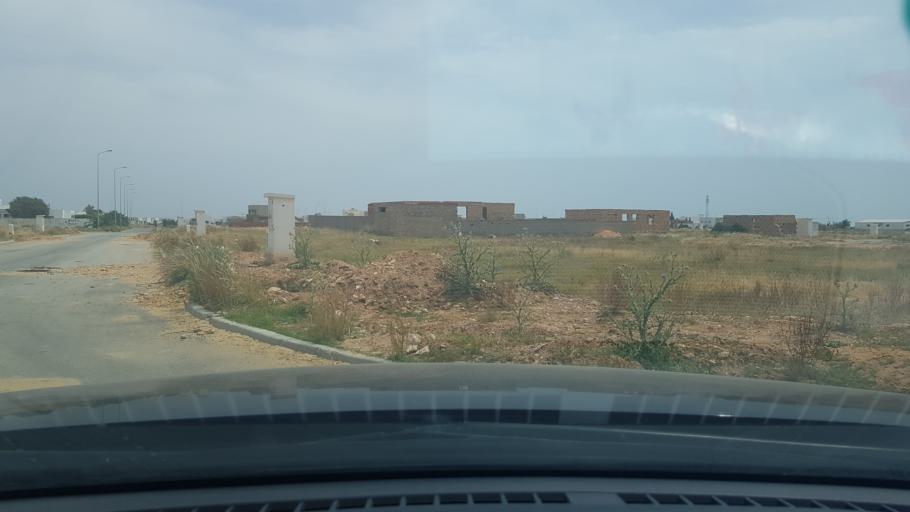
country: TN
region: Safaqis
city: Al Qarmadah
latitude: 34.8239
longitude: 10.7415
